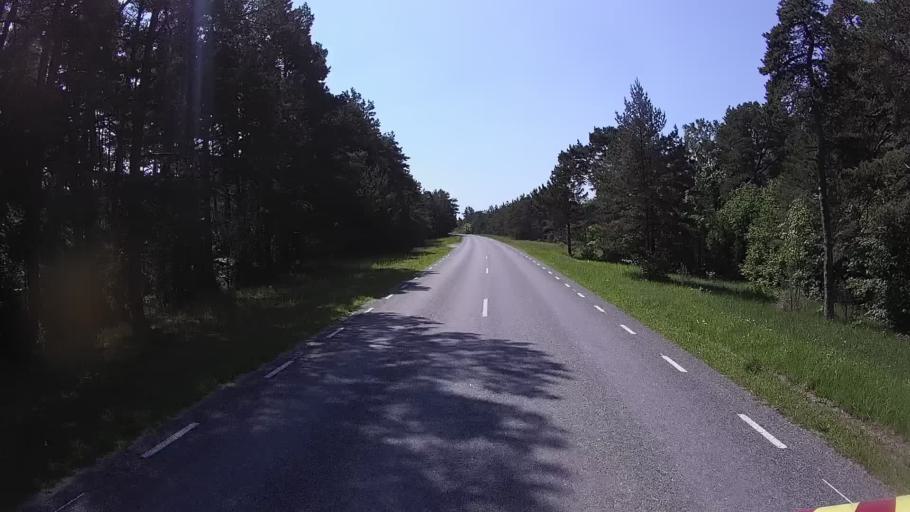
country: EE
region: Saare
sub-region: Kuressaare linn
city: Kuressaare
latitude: 58.1166
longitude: 22.2392
